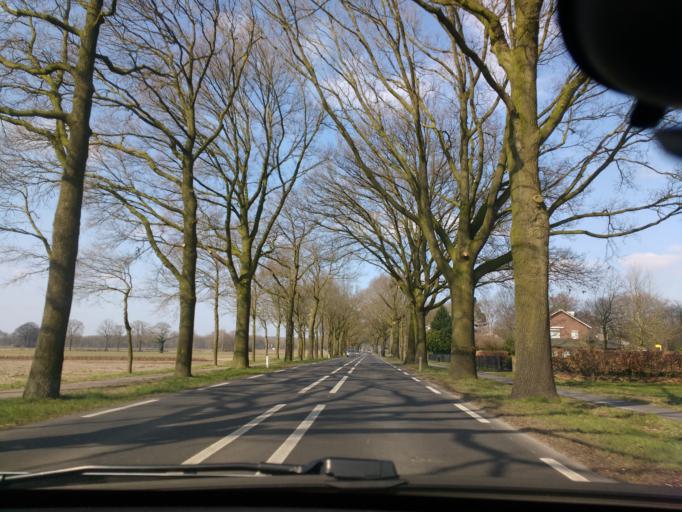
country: NL
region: Gelderland
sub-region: Gemeente Groesbeek
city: Bredeweg
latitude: 51.7280
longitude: 5.9416
